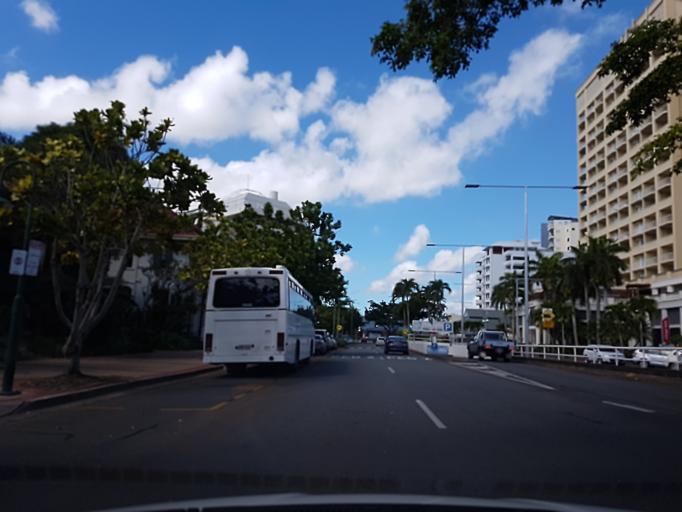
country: AU
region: Queensland
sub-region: Cairns
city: Cairns
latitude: -16.9234
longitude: 145.7787
